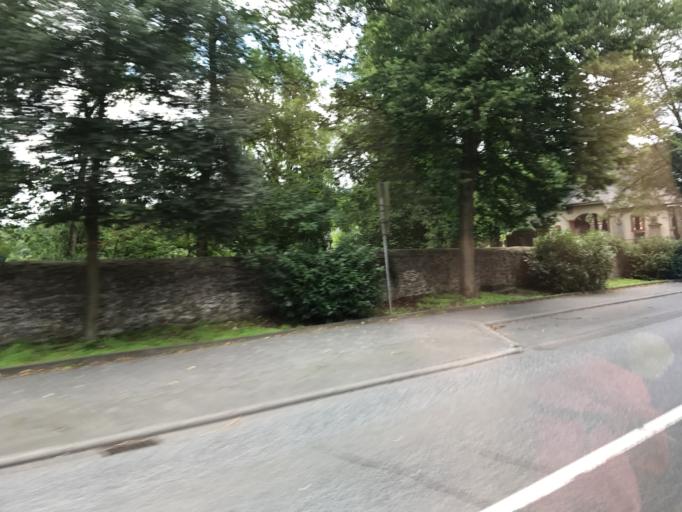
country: DE
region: Hesse
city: Weilburg
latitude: 50.4830
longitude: 8.2659
